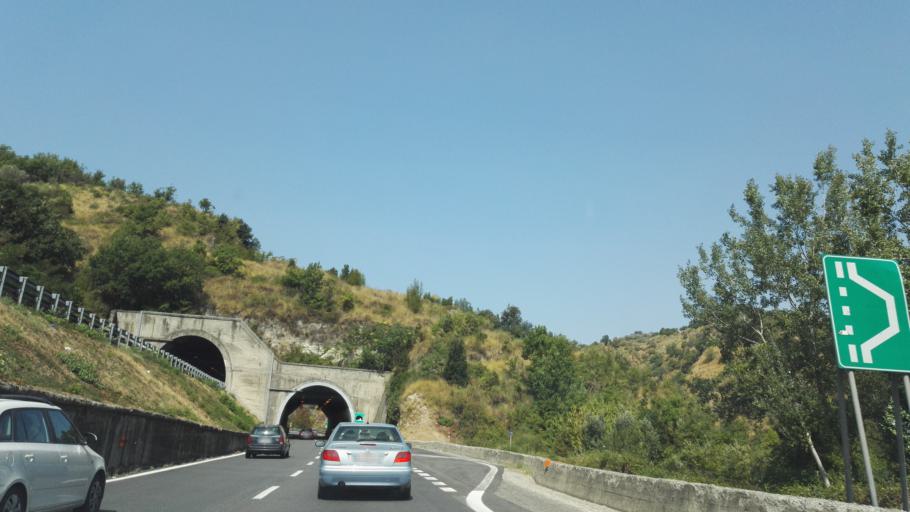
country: IT
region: Calabria
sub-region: Provincia di Cosenza
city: Donnici Inferiore
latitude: 39.2557
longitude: 16.2698
